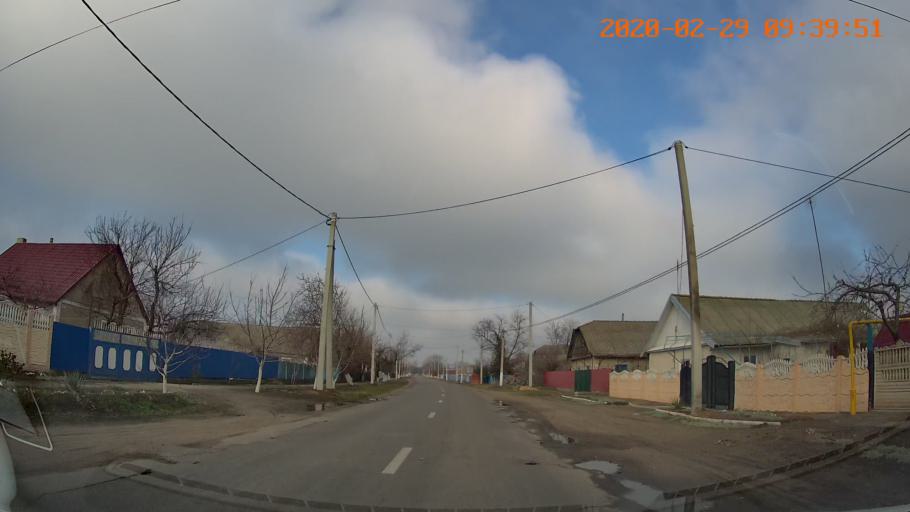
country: MD
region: Telenesti
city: Crasnoe
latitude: 46.6375
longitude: 29.8501
